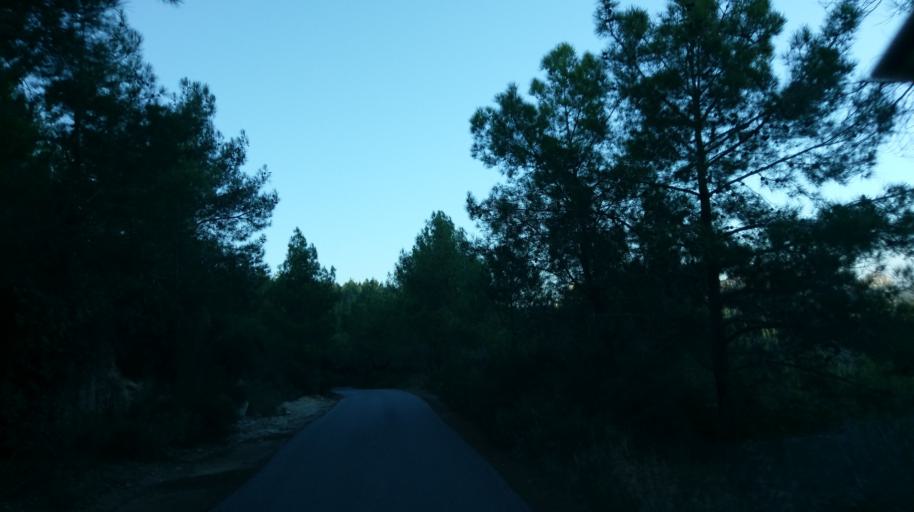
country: CY
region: Ammochostos
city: Trikomo
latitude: 35.3907
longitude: 33.9027
